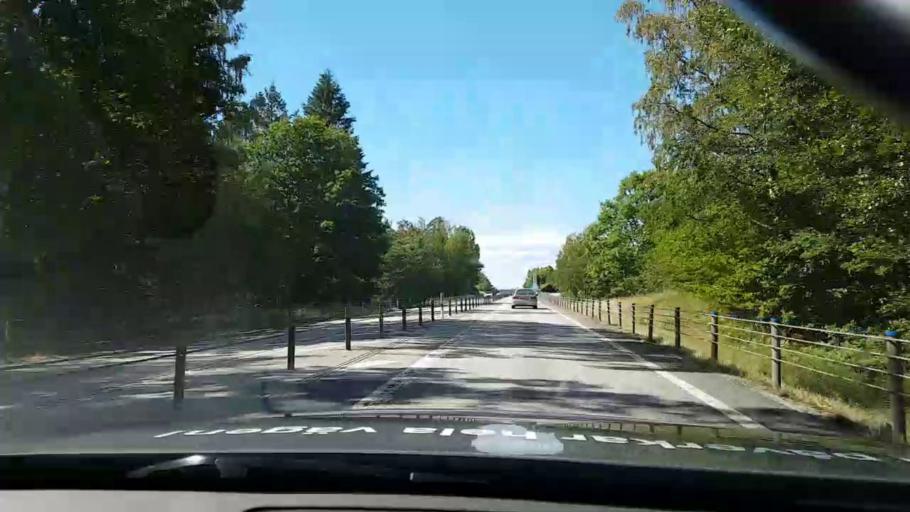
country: SE
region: Kalmar
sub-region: Vasterviks Kommun
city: Gamleby
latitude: 57.8664
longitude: 16.4182
